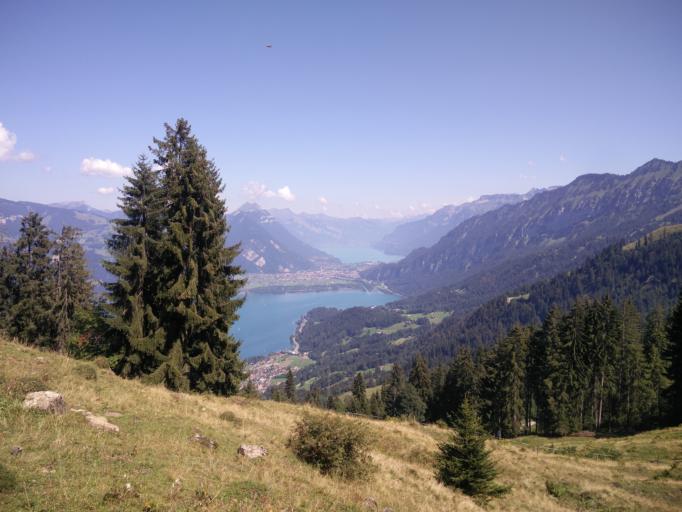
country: CH
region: Bern
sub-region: Frutigen-Niedersimmental District
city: Aeschi
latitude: 46.6387
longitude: 7.7480
